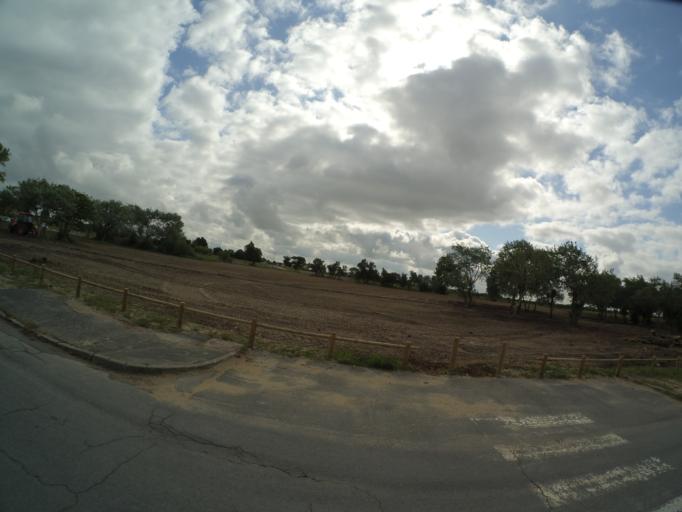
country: FR
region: Poitou-Charentes
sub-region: Departement de la Charente-Maritime
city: Angoulins
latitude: 46.1151
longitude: -1.1233
